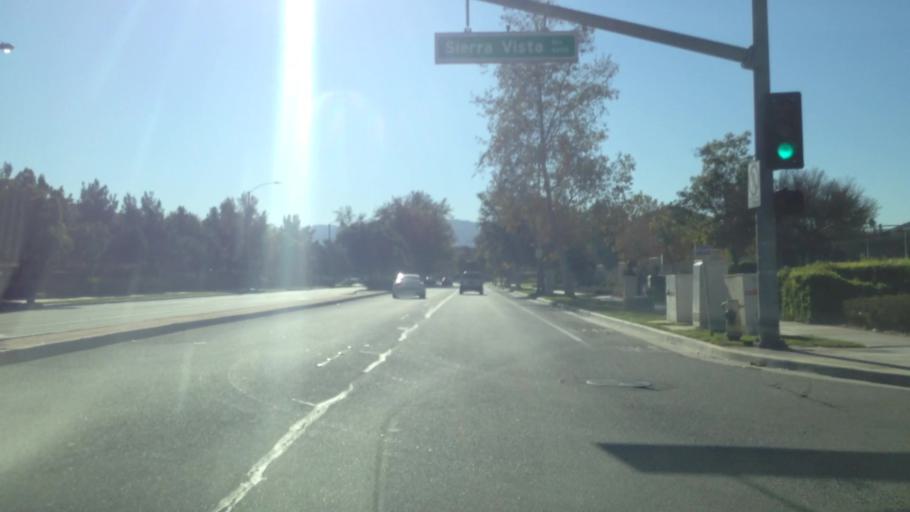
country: US
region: California
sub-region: Riverside County
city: Home Gardens
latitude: 33.9115
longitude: -117.4937
